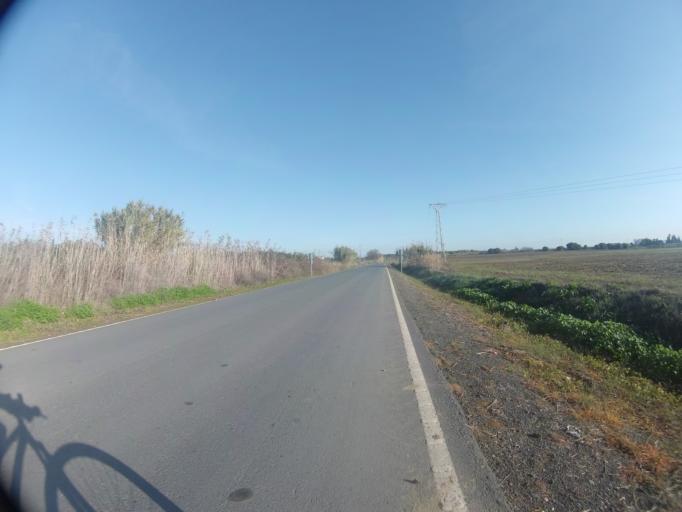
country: ES
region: Andalusia
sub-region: Provincia de Huelva
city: Huelva
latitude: 37.3162
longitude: -6.9140
